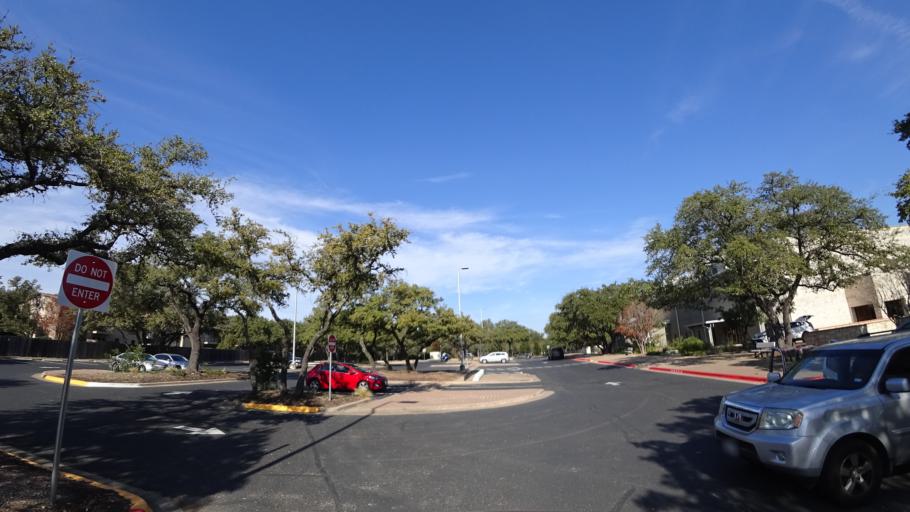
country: US
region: Texas
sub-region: Williamson County
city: Jollyville
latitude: 30.3744
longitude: -97.7571
